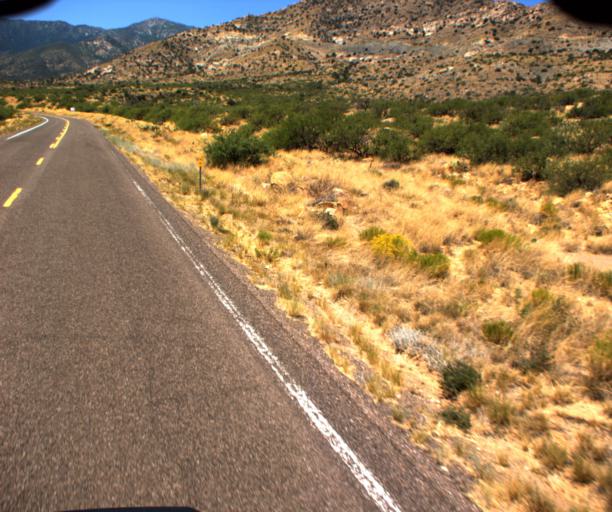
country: US
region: Arizona
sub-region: Graham County
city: Swift Trail Junction
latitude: 32.6851
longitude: -109.7675
